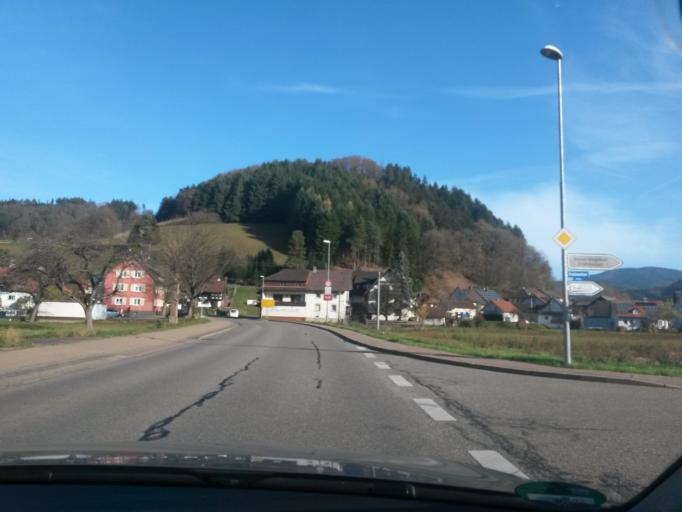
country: DE
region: Baden-Wuerttemberg
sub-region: Freiburg Region
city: Elzach
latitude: 48.1527
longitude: 8.0379
